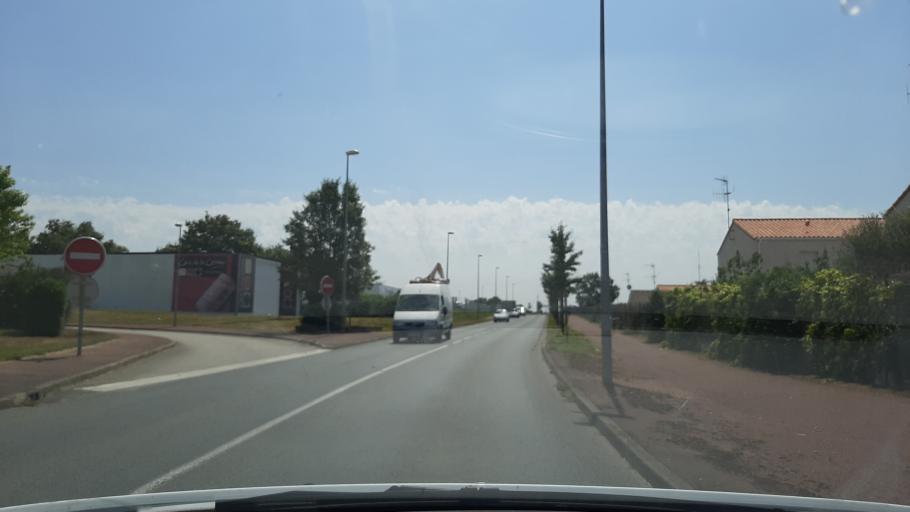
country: FR
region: Pays de la Loire
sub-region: Departement de la Vendee
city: Le Poire-sur-Vie
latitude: 46.7655
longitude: -1.4974
